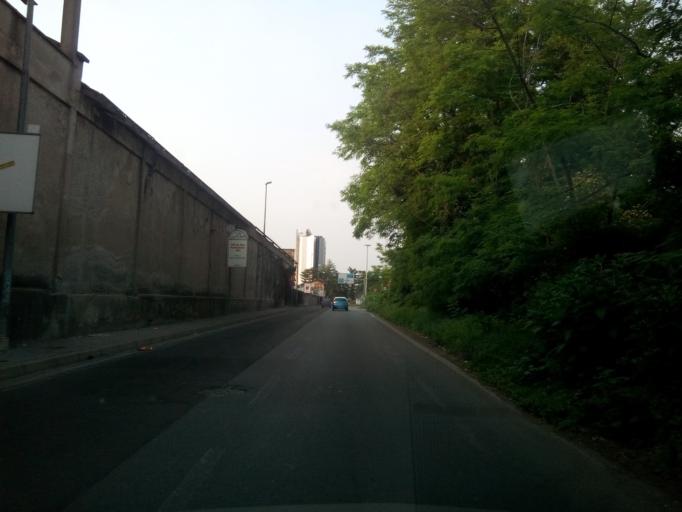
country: IT
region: Lombardy
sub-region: Citta metropolitana di Milano
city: Cerro Maggiore
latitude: 45.5984
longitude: 8.9432
